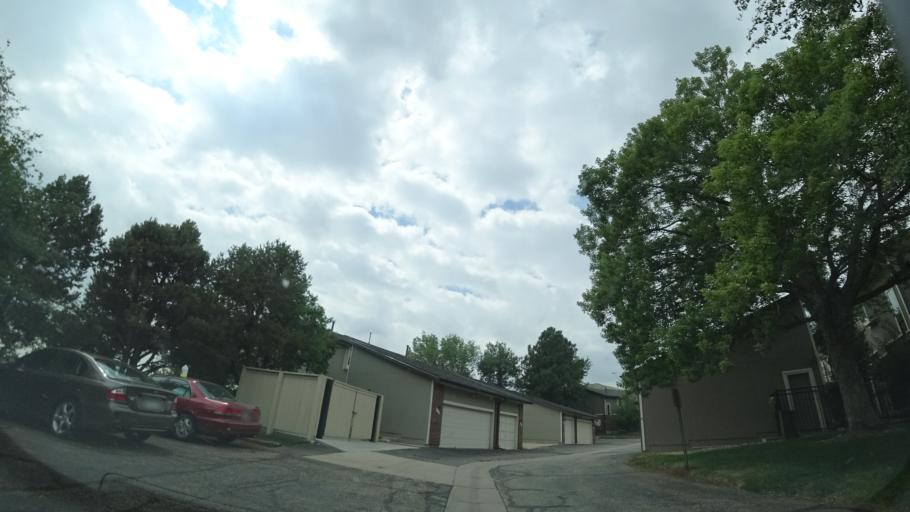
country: US
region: Colorado
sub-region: Jefferson County
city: West Pleasant View
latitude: 39.7139
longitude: -105.1617
